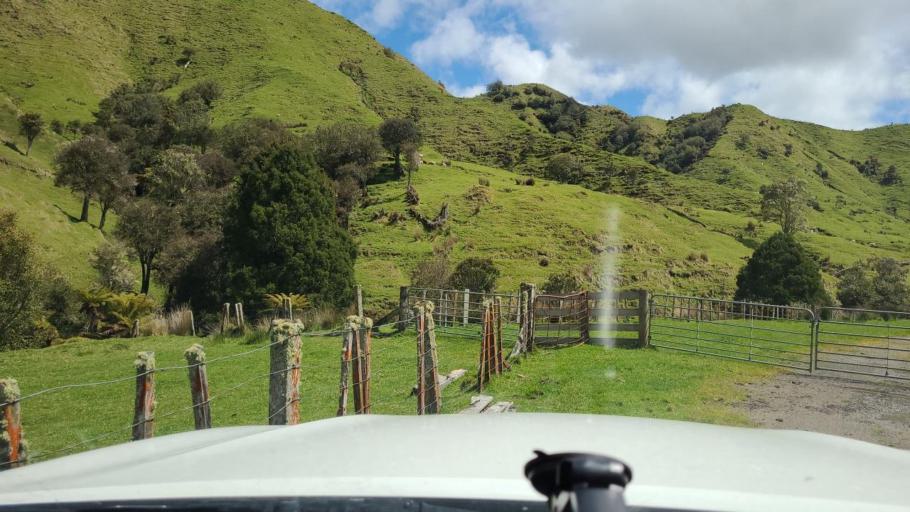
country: NZ
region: Bay of Plenty
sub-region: Opotiki District
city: Opotiki
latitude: -38.2115
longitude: 177.5887
